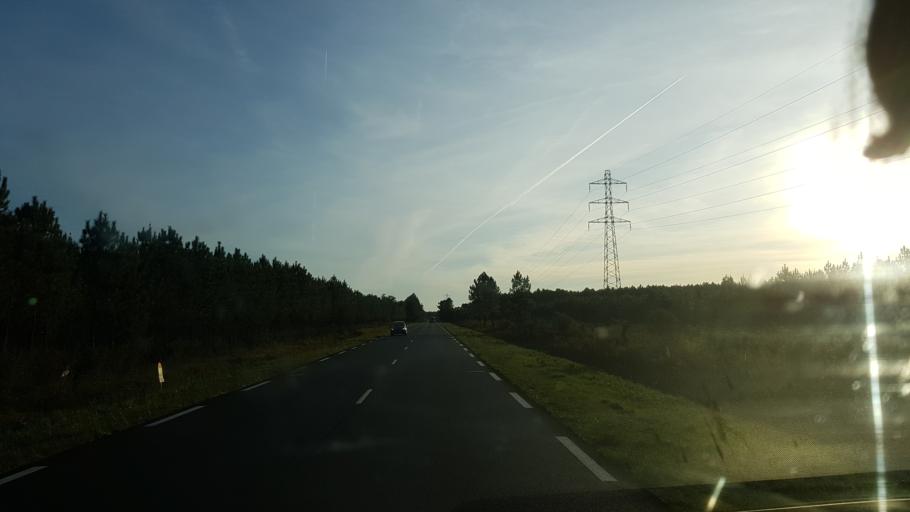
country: FR
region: Aquitaine
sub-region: Departement de la Gironde
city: Martignas-sur-Jalle
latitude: 44.8047
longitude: -0.8647
